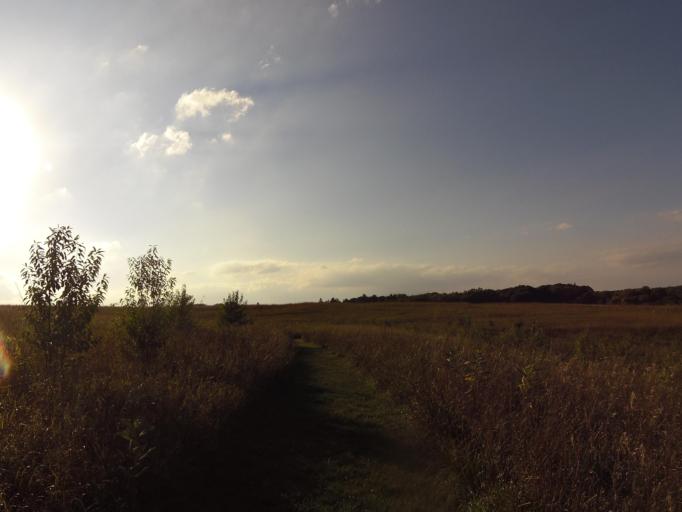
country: US
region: Minnesota
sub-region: Washington County
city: Lake Saint Croix Beach
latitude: 44.9362
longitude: -92.7924
